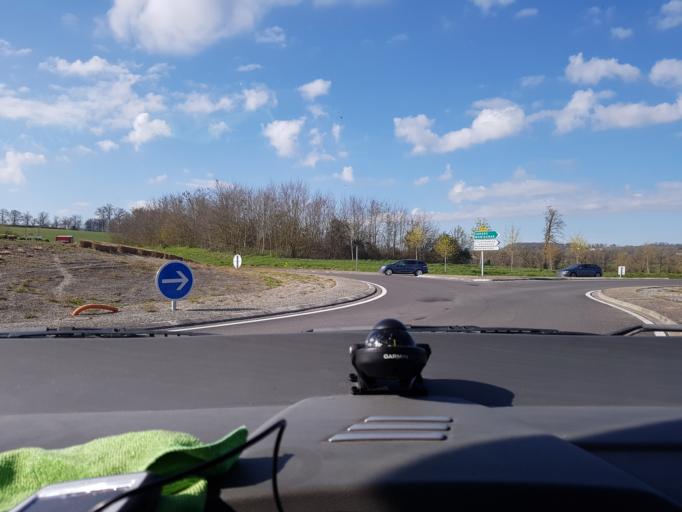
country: FR
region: Midi-Pyrenees
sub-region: Departement de l'Aveyron
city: Colombies
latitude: 44.3987
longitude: 2.3010
